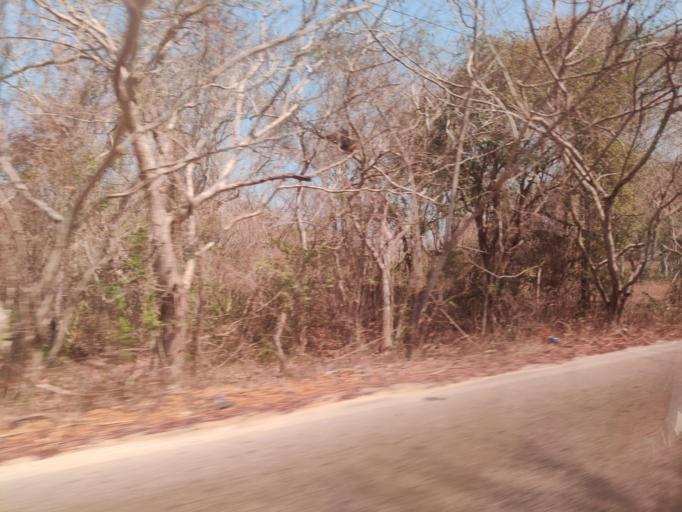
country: CO
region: Bolivar
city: Turbana
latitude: 10.2135
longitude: -75.5981
